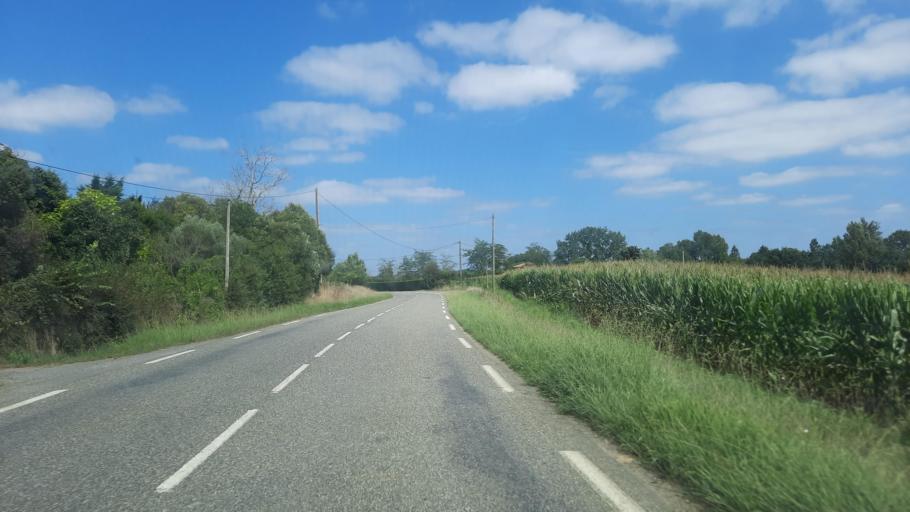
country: FR
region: Midi-Pyrenees
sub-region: Departement du Gers
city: Lombez
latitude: 43.4284
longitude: 0.8352
